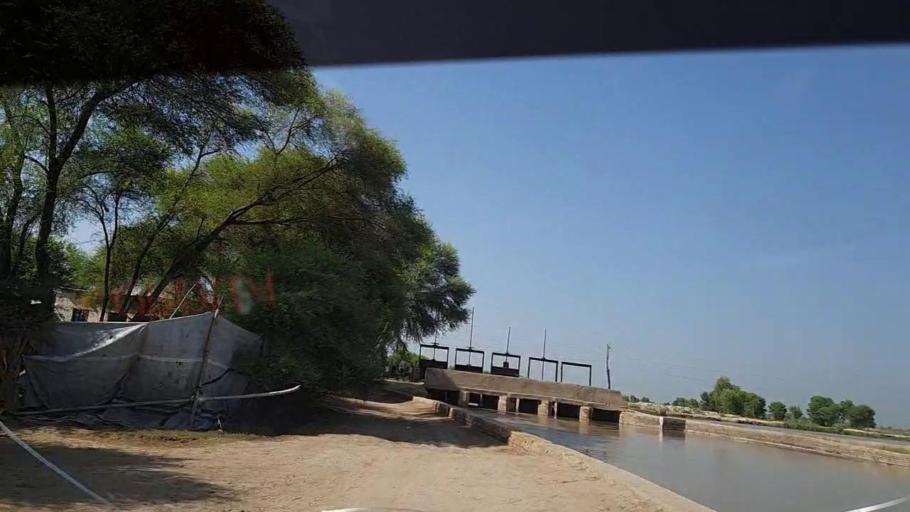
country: PK
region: Sindh
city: Ghauspur
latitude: 28.1748
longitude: 69.0993
